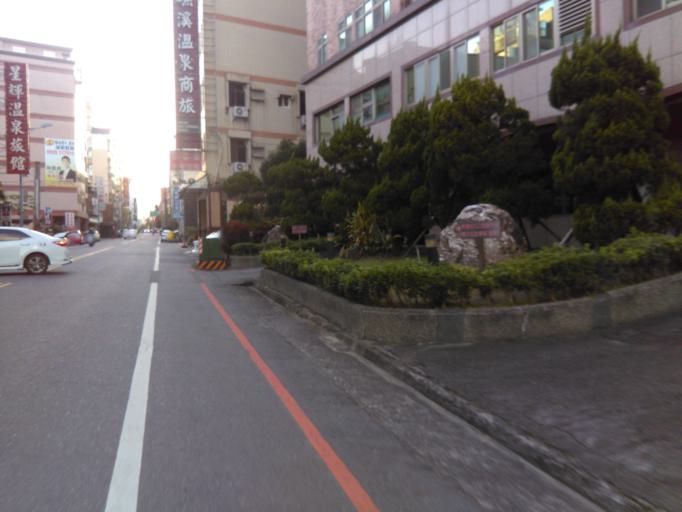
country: TW
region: Taiwan
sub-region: Yilan
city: Yilan
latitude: 24.8275
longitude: 121.7655
